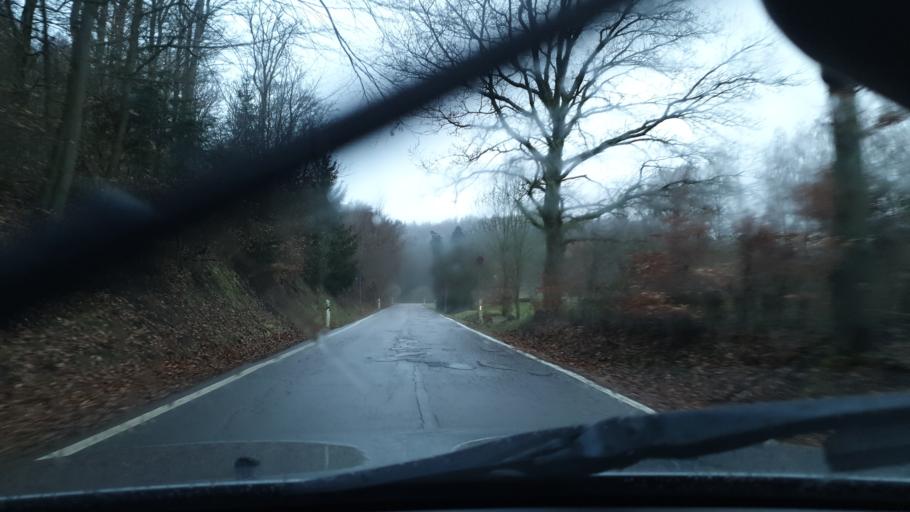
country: DE
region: Rheinland-Pfalz
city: Kaiserslautern
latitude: 49.4167
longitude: 7.7659
